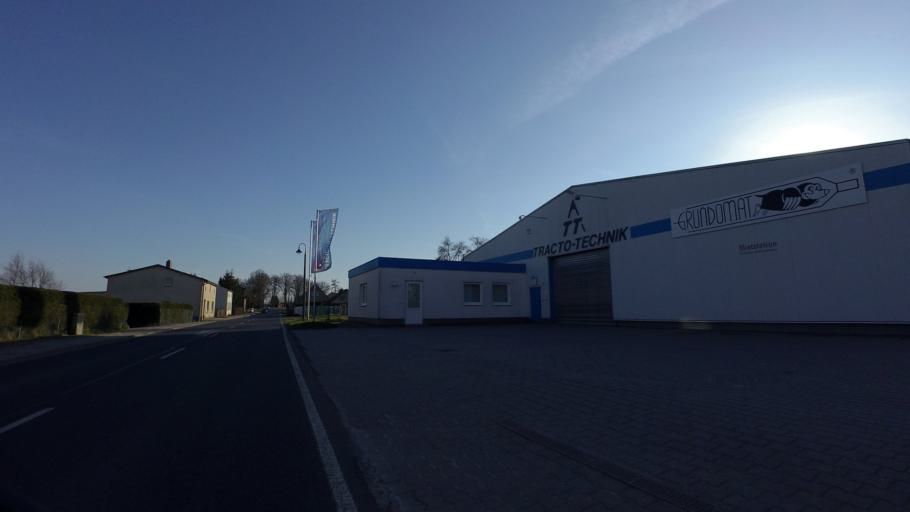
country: DE
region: Brandenburg
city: Britz
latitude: 52.9106
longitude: 13.8027
